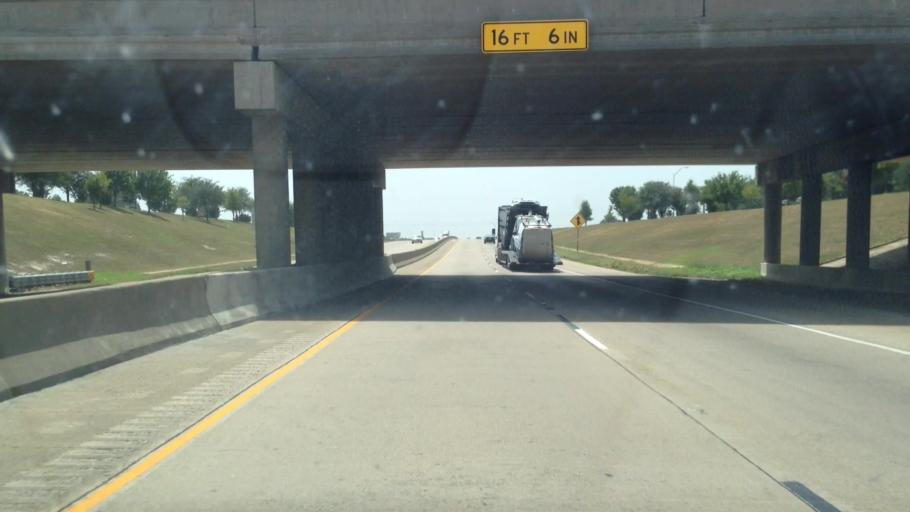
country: US
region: Texas
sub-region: Hopkins County
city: Sulphur Springs
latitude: 33.1164
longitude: -95.5961
